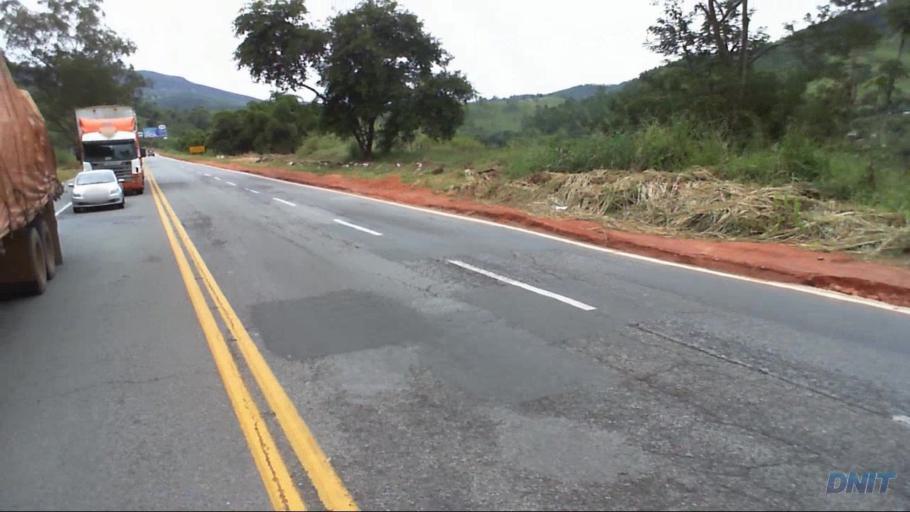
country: BR
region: Minas Gerais
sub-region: Joao Monlevade
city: Joao Monlevade
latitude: -19.8593
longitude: -43.2311
